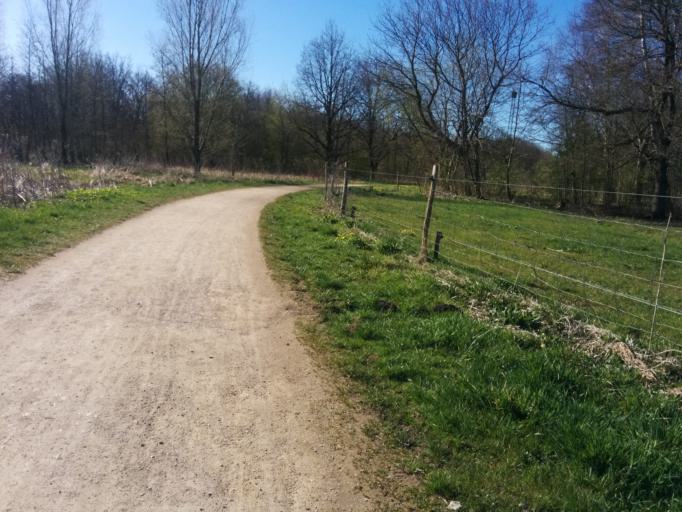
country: DK
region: North Denmark
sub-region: Alborg Kommune
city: Aalborg
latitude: 57.0215
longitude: 9.9151
